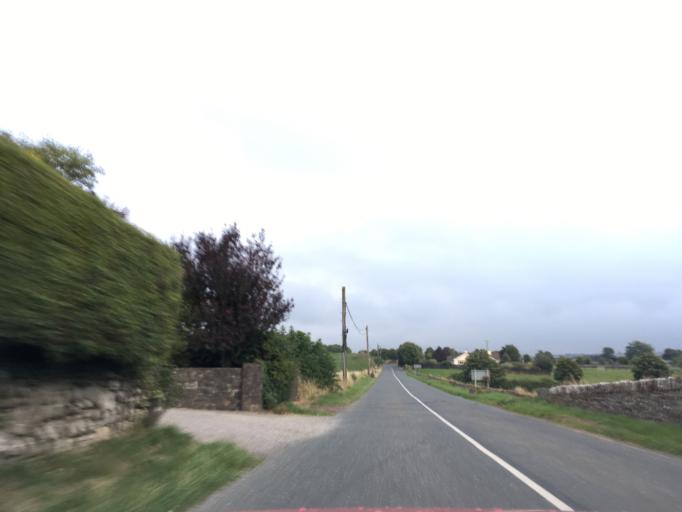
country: IE
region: Munster
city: Cashel
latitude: 52.4969
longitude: -7.9770
